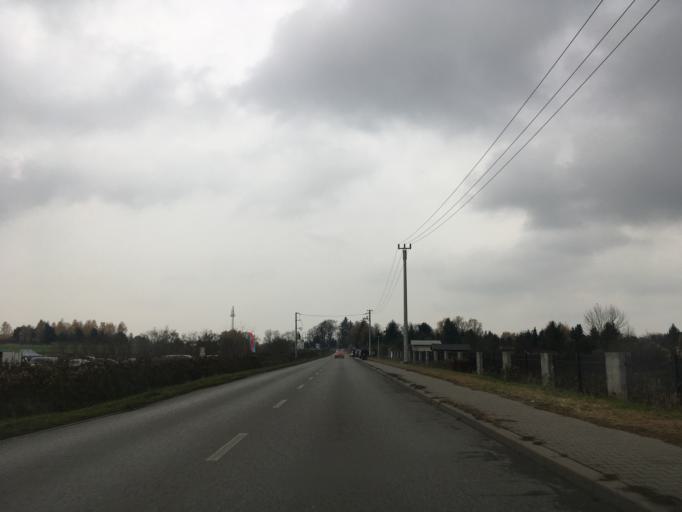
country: PL
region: Masovian Voivodeship
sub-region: Powiat piaseczynski
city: Zalesie Gorne
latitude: 52.0448
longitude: 21.0041
